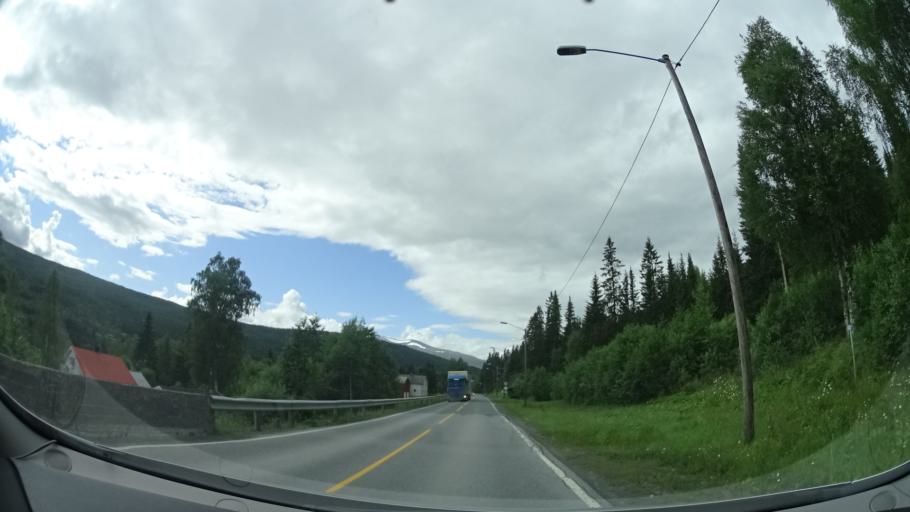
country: NO
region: Nord-Trondelag
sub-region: Meraker
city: Meraker
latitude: 63.3974
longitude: 11.7968
